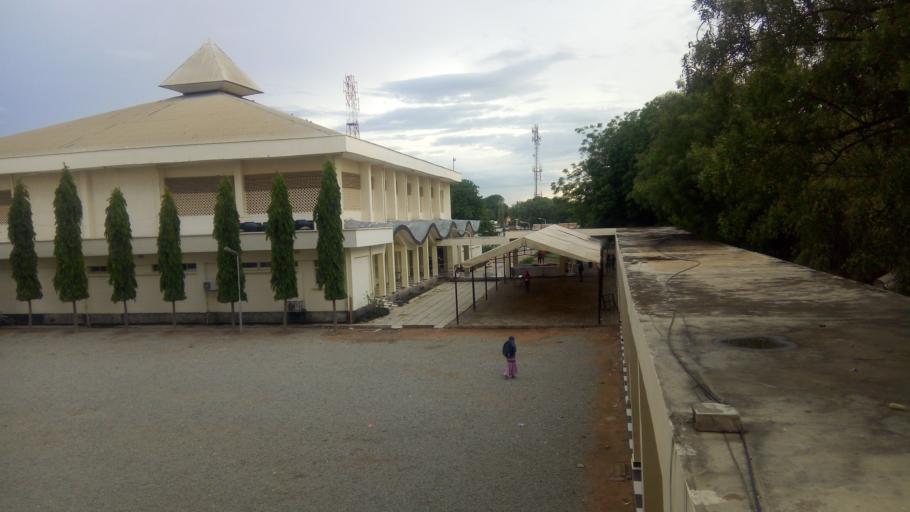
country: TZ
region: Dodoma
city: Dodoma
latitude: -6.1215
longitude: 35.7454
